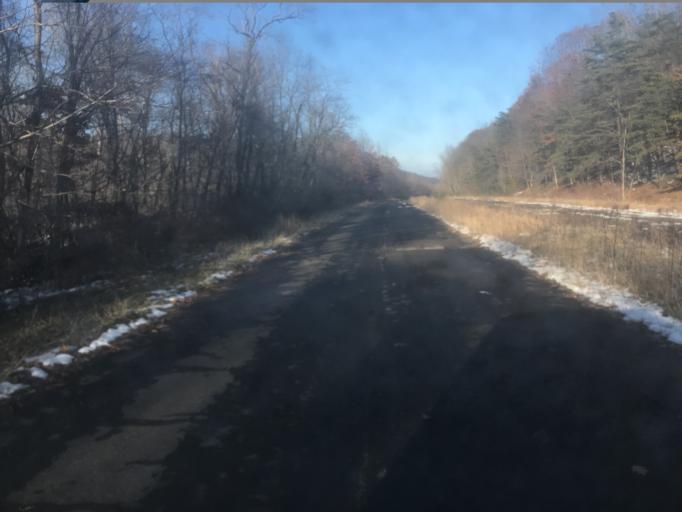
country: US
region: Pennsylvania
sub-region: Bedford County
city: Earlston
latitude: 40.0311
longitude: -78.1844
